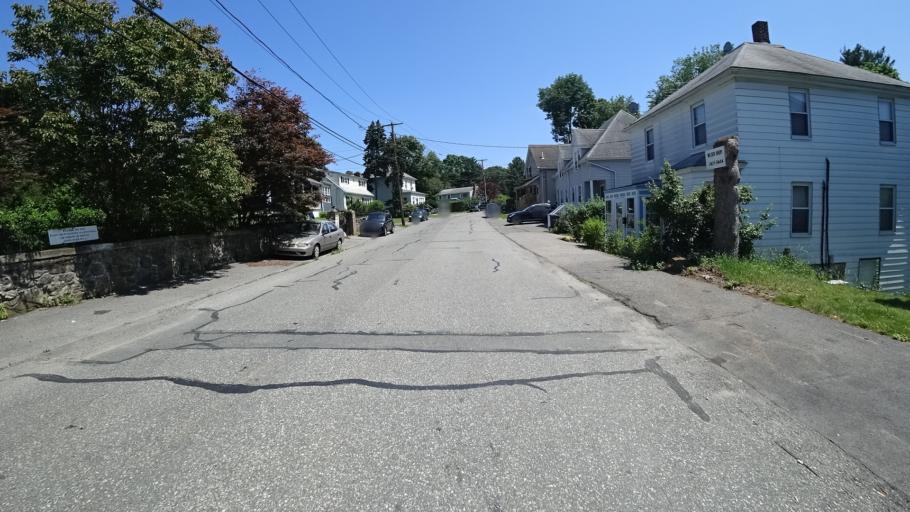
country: US
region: Massachusetts
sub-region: Norfolk County
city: Dedham
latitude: 42.2513
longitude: -71.1527
